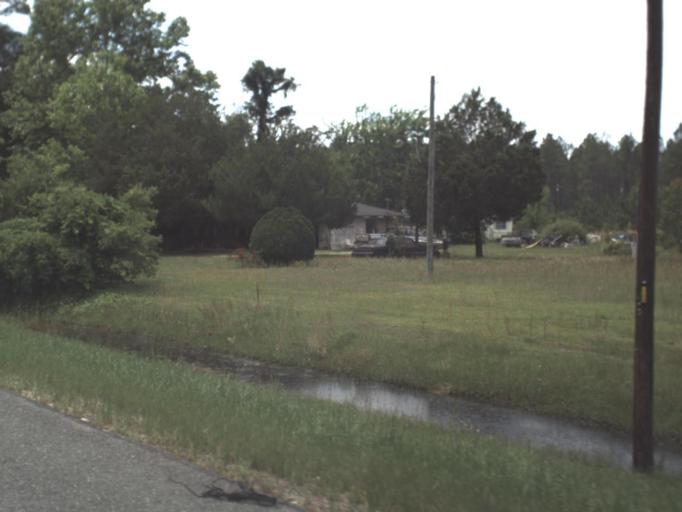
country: US
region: Florida
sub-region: Calhoun County
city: Blountstown
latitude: 30.3577
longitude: -85.1053
